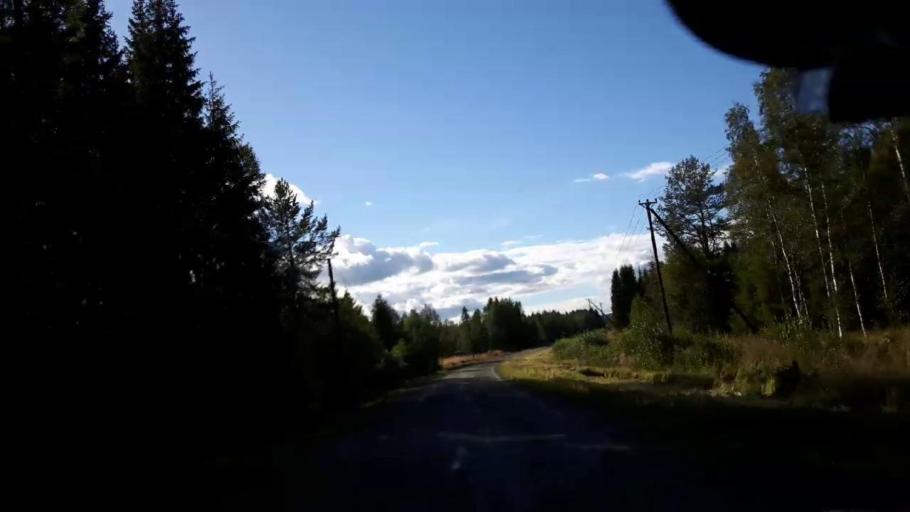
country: SE
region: Jaemtland
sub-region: Ragunda Kommun
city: Hammarstrand
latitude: 63.4895
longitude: 16.0605
